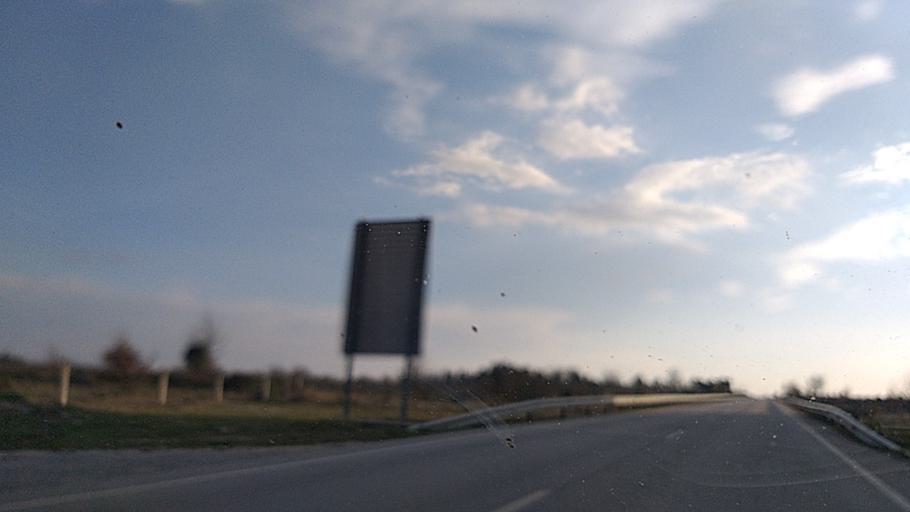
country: ES
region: Castille and Leon
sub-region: Provincia de Salamanca
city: Fuentes de Onoro
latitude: 40.6036
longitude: -6.9856
